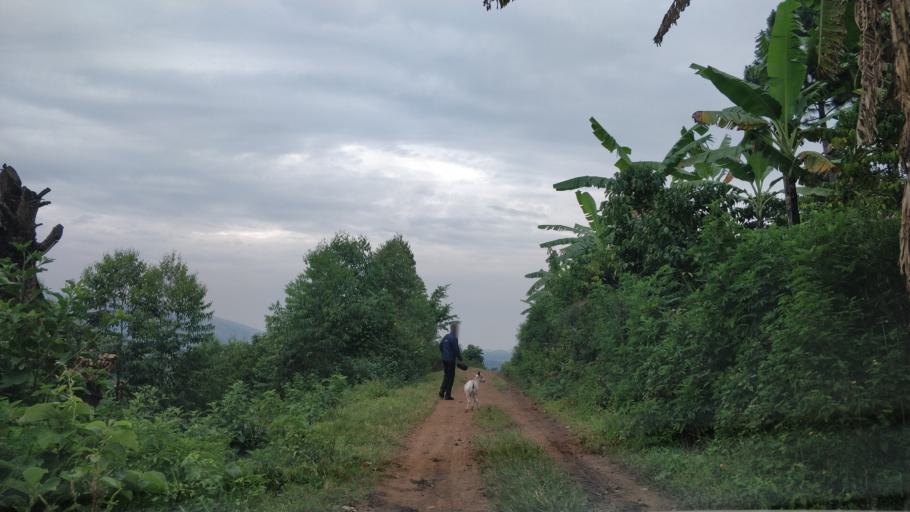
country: UG
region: Western Region
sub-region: Sheema District
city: Kibingo
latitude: -0.7025
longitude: 30.3963
